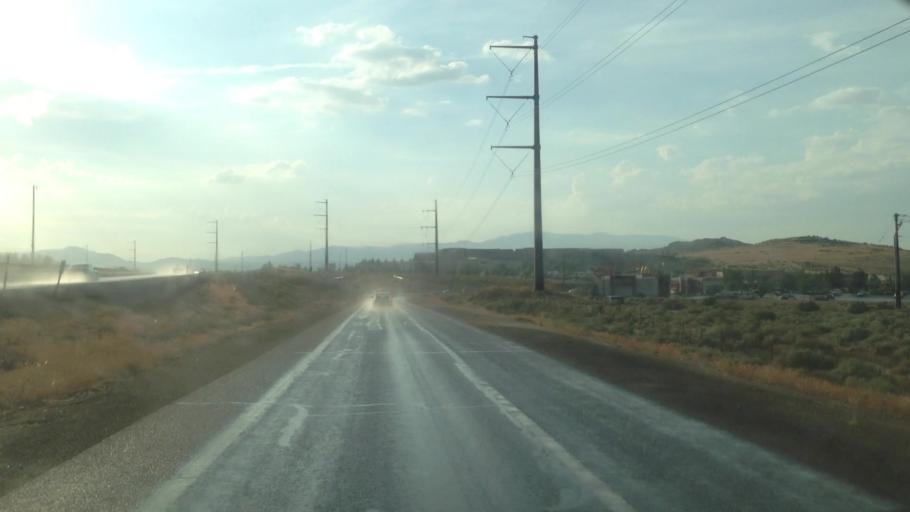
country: US
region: Nevada
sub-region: Washoe County
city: Golden Valley
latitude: 39.6093
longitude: -119.8476
